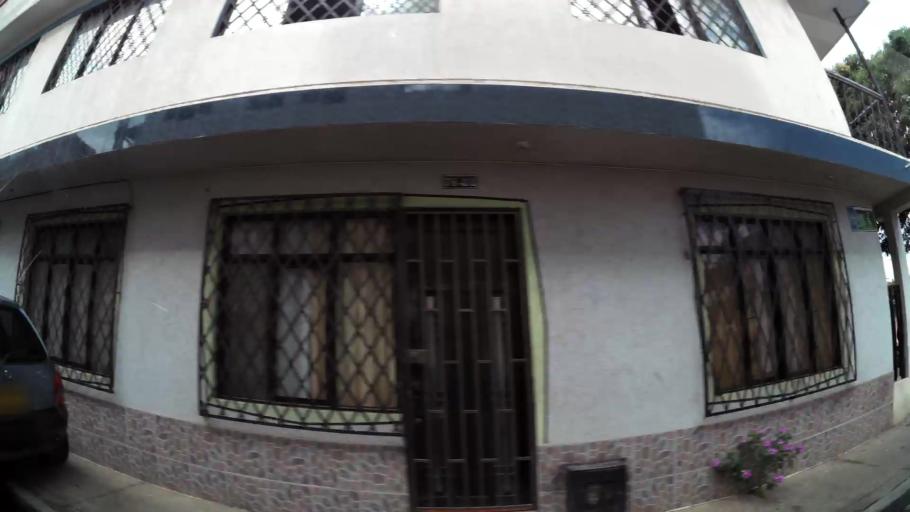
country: CO
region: Valle del Cauca
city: Cali
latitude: 3.3893
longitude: -76.5502
